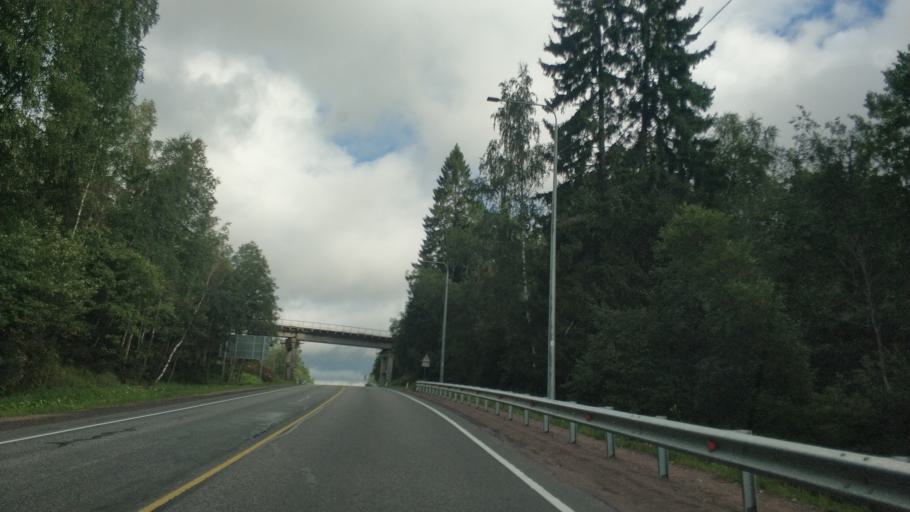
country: RU
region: Republic of Karelia
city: Khelyulya
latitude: 61.7773
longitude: 30.6610
